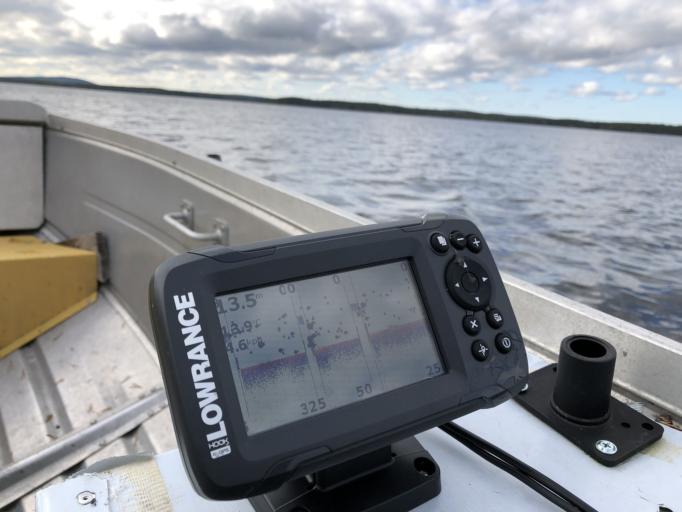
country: FI
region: Lapland
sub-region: Itae-Lappi
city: Posio
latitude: 66.1068
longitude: 28.5023
